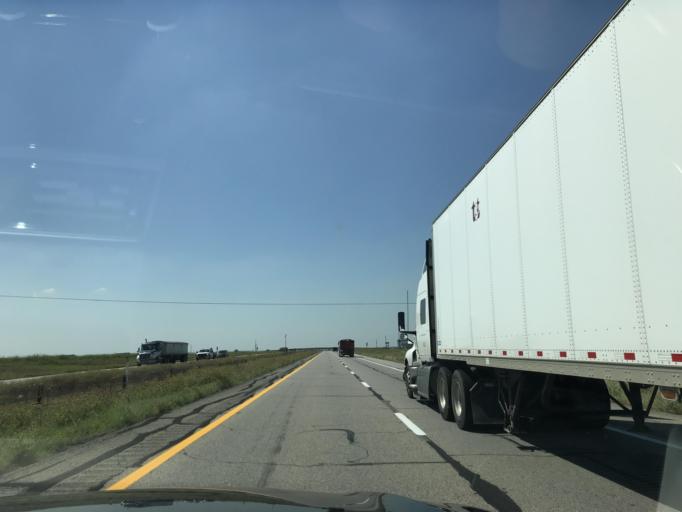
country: US
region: Texas
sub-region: Johnson County
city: Grandview
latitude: 32.3309
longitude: -97.1890
